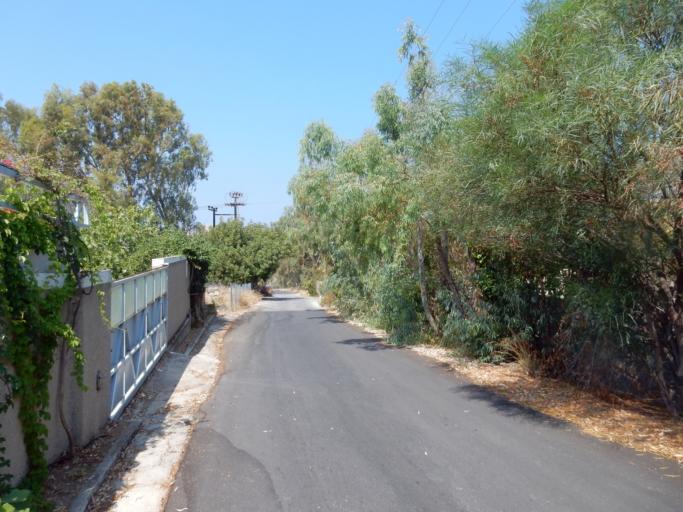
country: GR
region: Attica
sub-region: Nomos Piraios
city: Aegina
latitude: 37.6905
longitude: 23.4668
